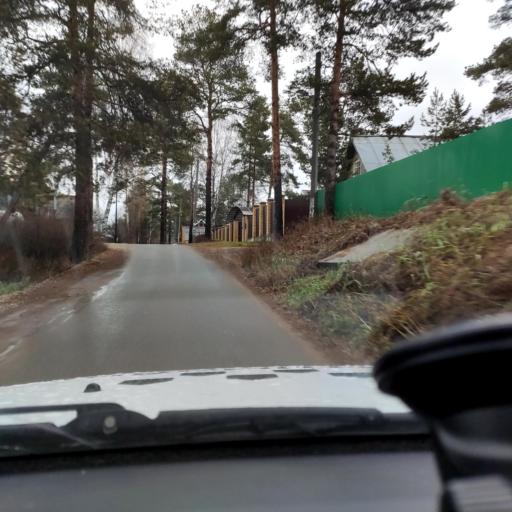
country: RU
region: Perm
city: Perm
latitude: 58.0591
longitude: 56.3037
